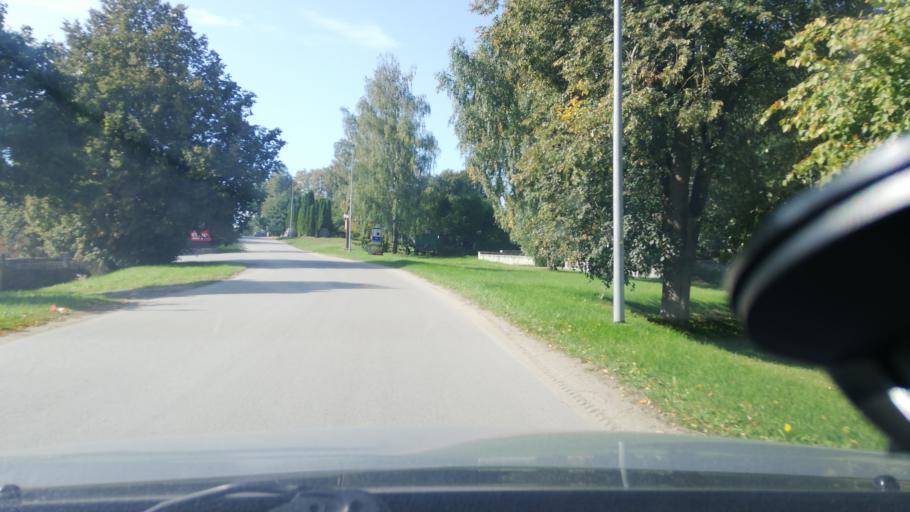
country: LT
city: Salantai
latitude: 55.9175
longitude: 21.4685
